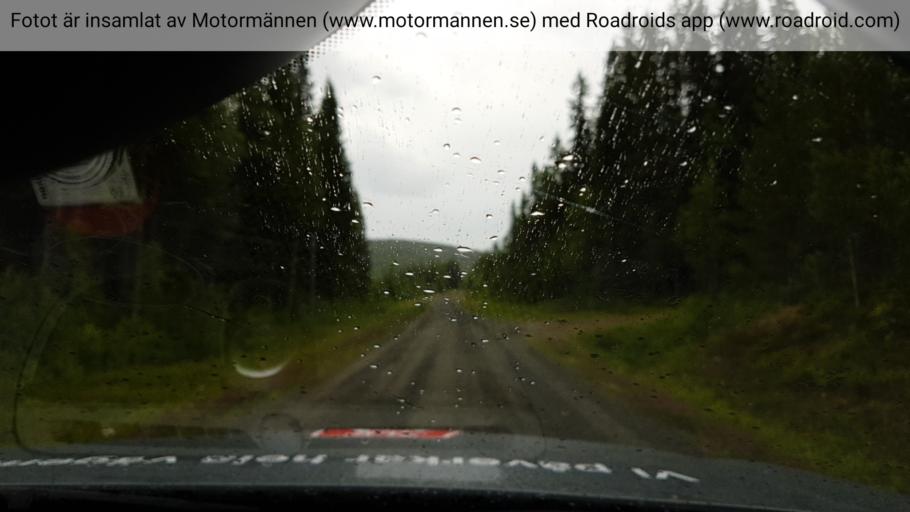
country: SE
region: Jaemtland
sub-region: Bergs Kommun
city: Hoverberg
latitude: 62.5348
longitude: 14.7035
